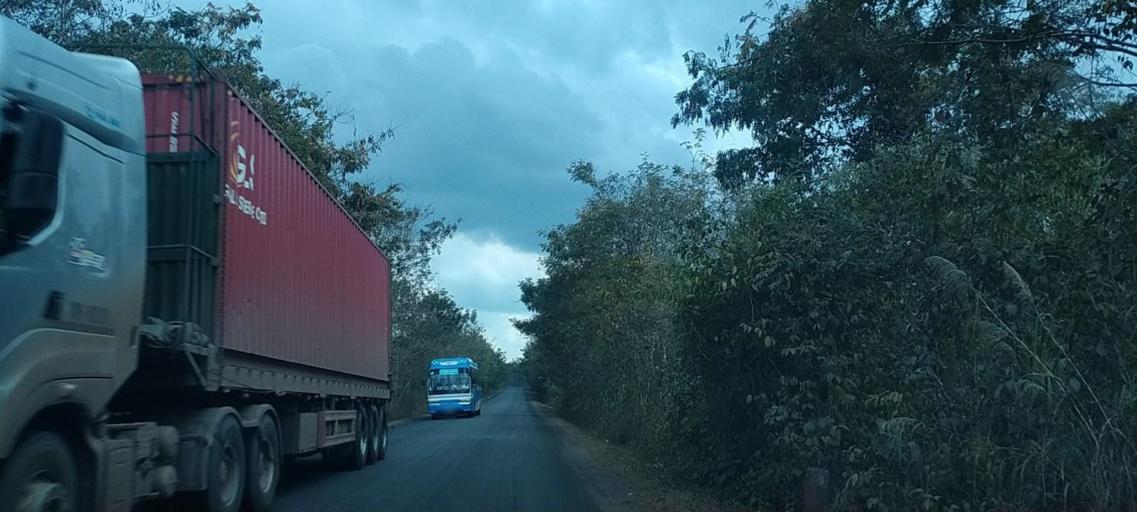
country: TH
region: Nakhon Phanom
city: Ban Phaeng
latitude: 17.8425
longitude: 104.4394
